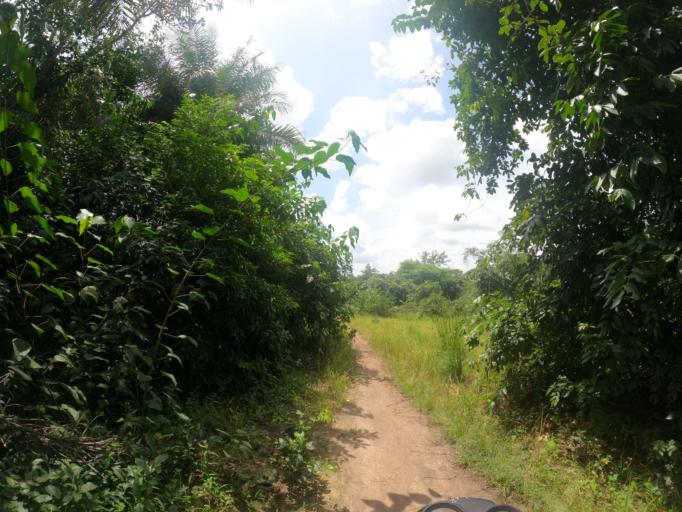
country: SL
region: Northern Province
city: Makeni
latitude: 9.1321
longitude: -12.2736
